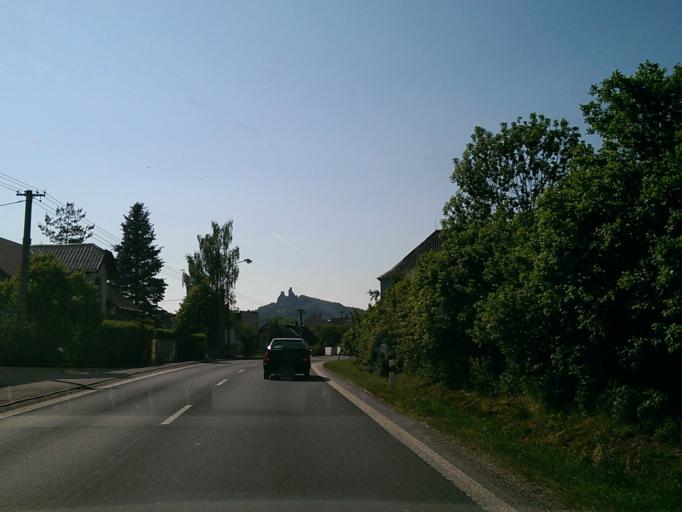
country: CZ
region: Liberecky
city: Rovensko pod Troskami
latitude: 50.5081
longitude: 15.2659
